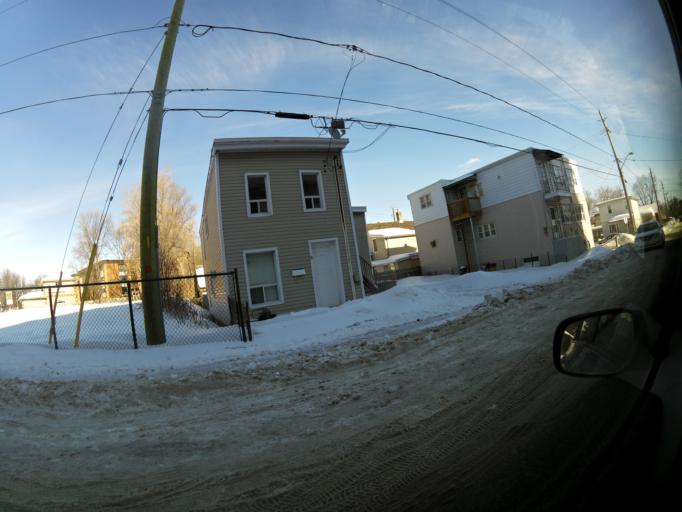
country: CA
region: Ontario
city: Ottawa
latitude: 45.4439
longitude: -75.6701
